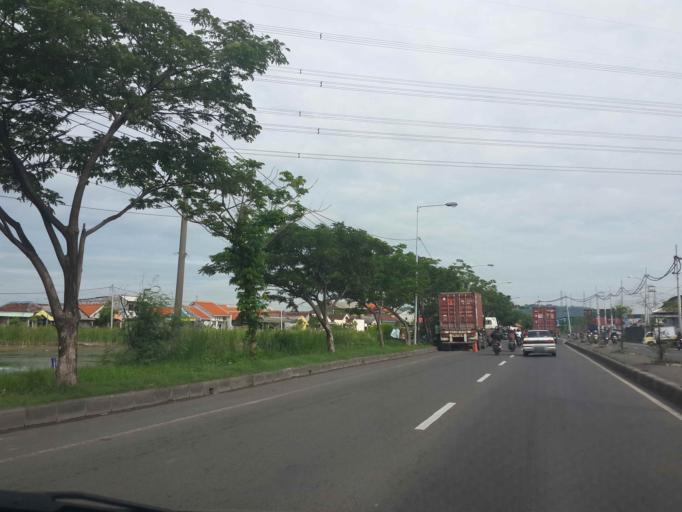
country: ID
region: East Java
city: Kebomas
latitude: -7.2005
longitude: 112.6487
